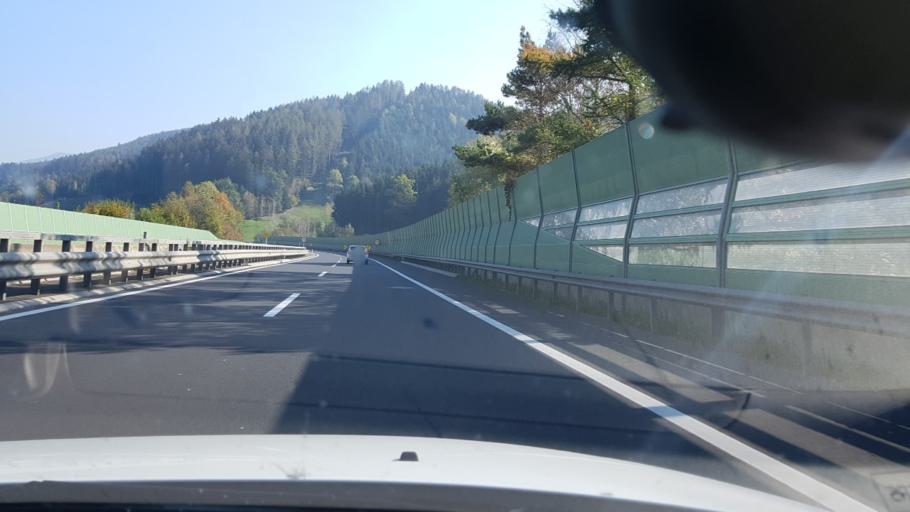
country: AT
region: Styria
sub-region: Politischer Bezirk Bruck-Muerzzuschlag
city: Oberaich
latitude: 47.3975
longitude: 15.2328
